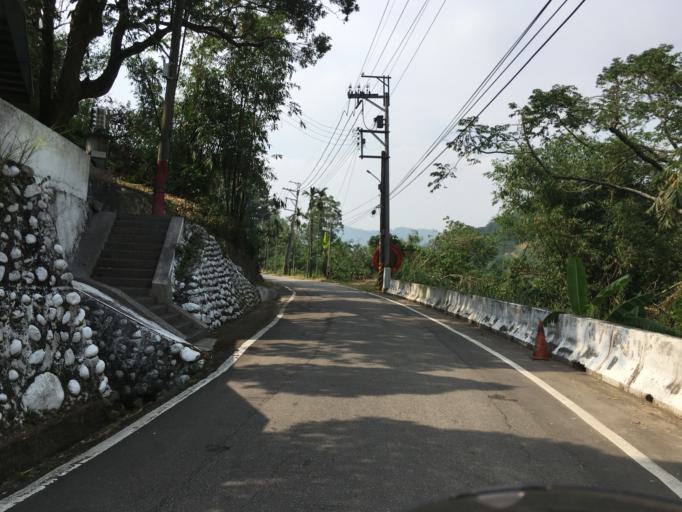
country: TW
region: Taiwan
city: Fengyuan
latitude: 24.1851
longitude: 120.7632
